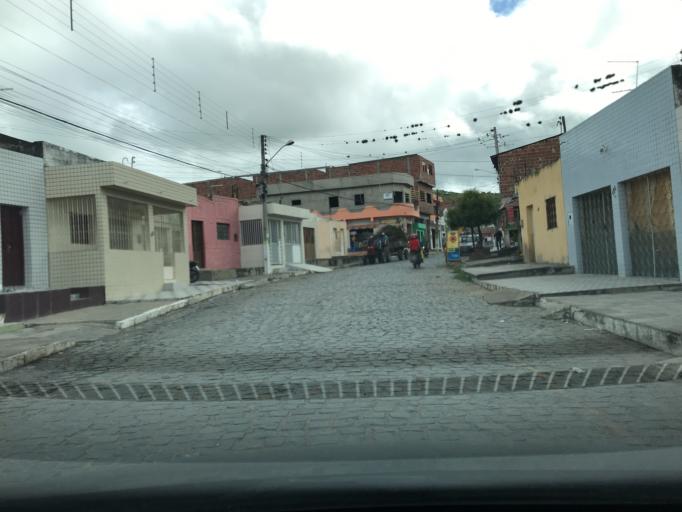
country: BR
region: Pernambuco
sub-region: Bezerros
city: Bezerros
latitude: -8.2319
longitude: -35.7587
